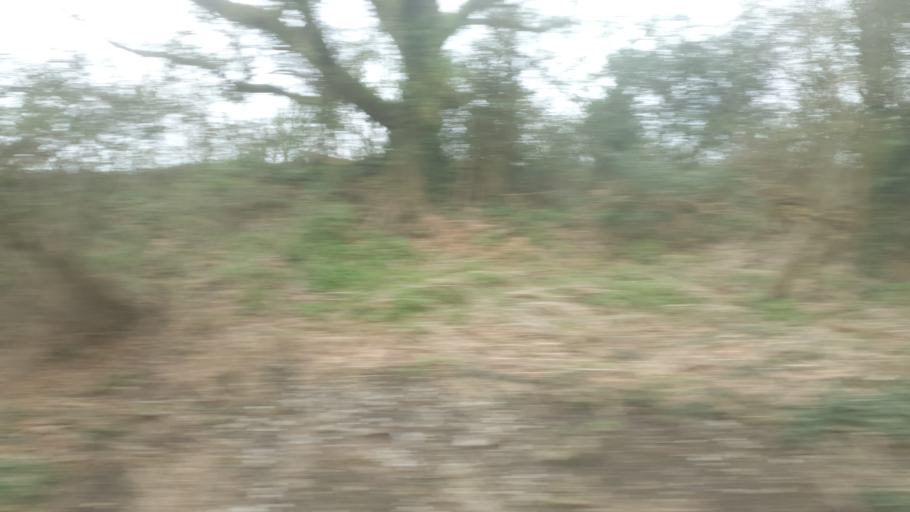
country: GB
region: England
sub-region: West Sussex
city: Pulborough
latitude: 50.9372
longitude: -0.5415
